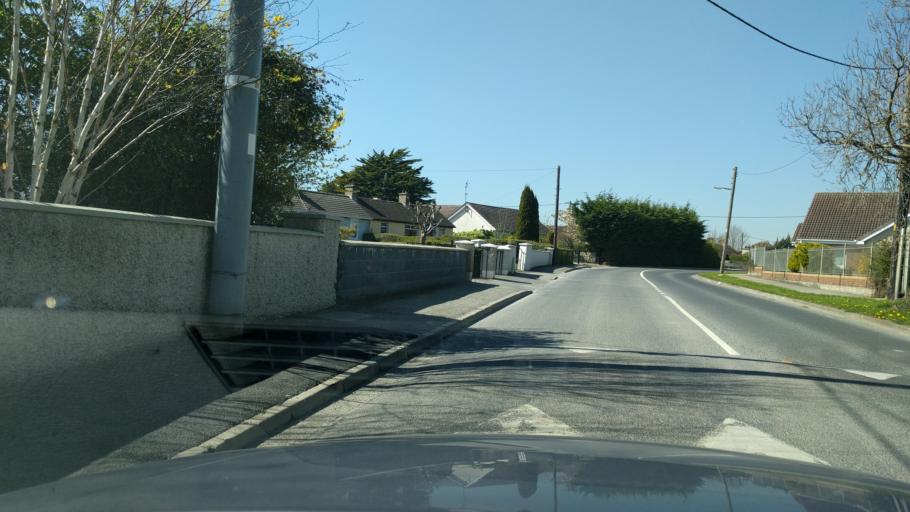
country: IE
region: Leinster
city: Firhouse
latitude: 53.2703
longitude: -6.3432
